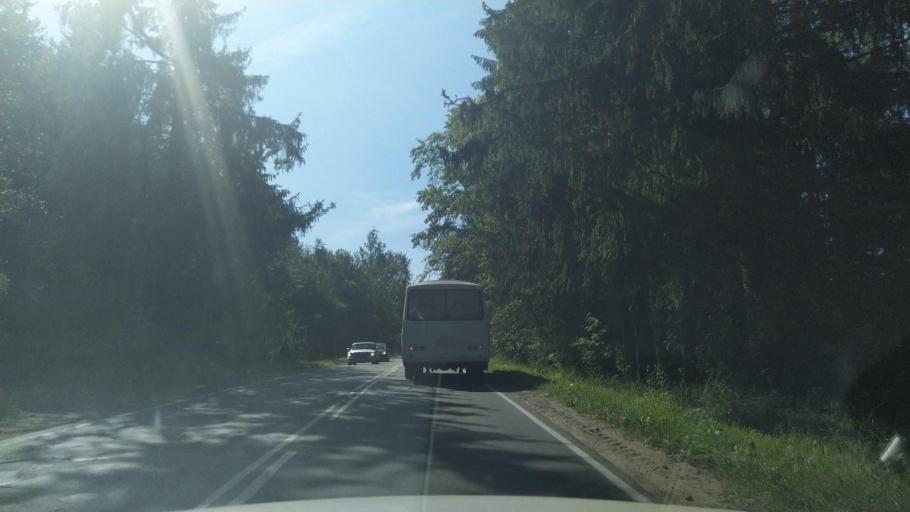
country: RU
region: Leningrad
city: Siverskiy
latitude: 59.3284
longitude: 30.0646
